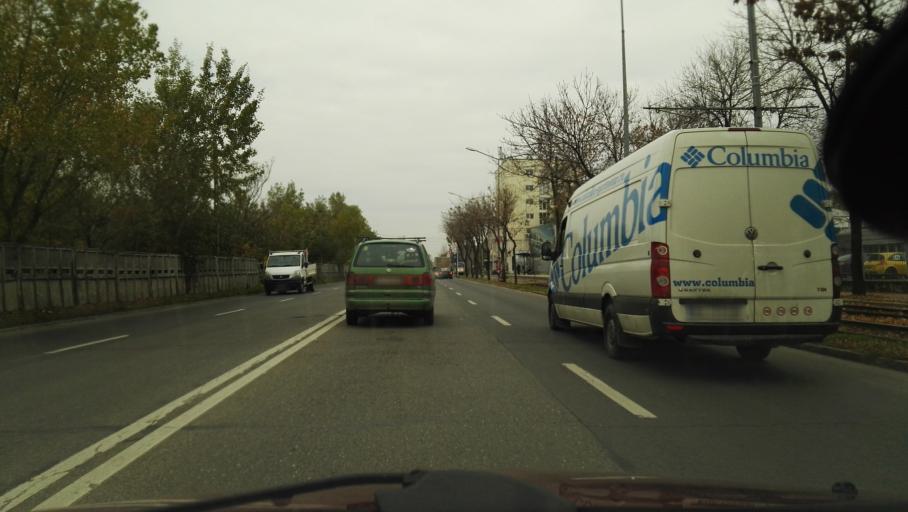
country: RO
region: Bucuresti
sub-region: Municipiul Bucuresti
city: Bucuresti
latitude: 44.4104
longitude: 26.0847
